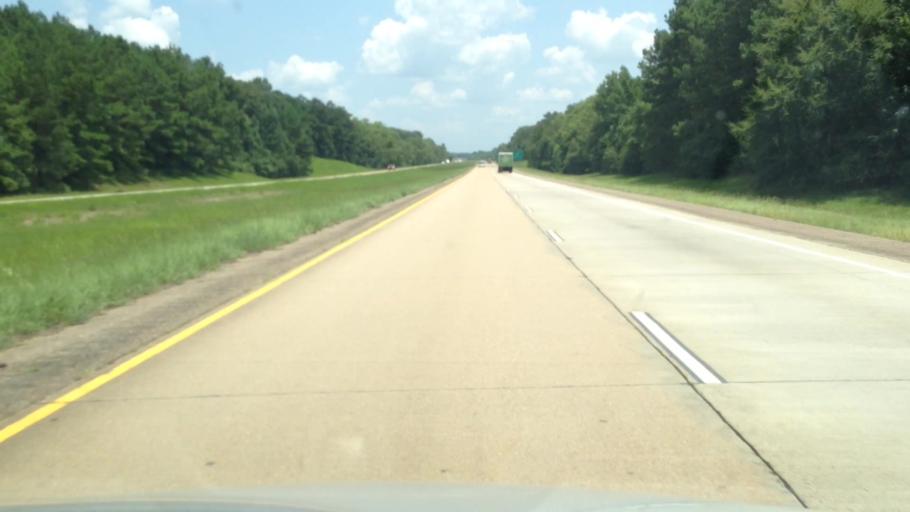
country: US
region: Louisiana
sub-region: Rapides Parish
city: Lecompte
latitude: 31.0252
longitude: -92.3995
